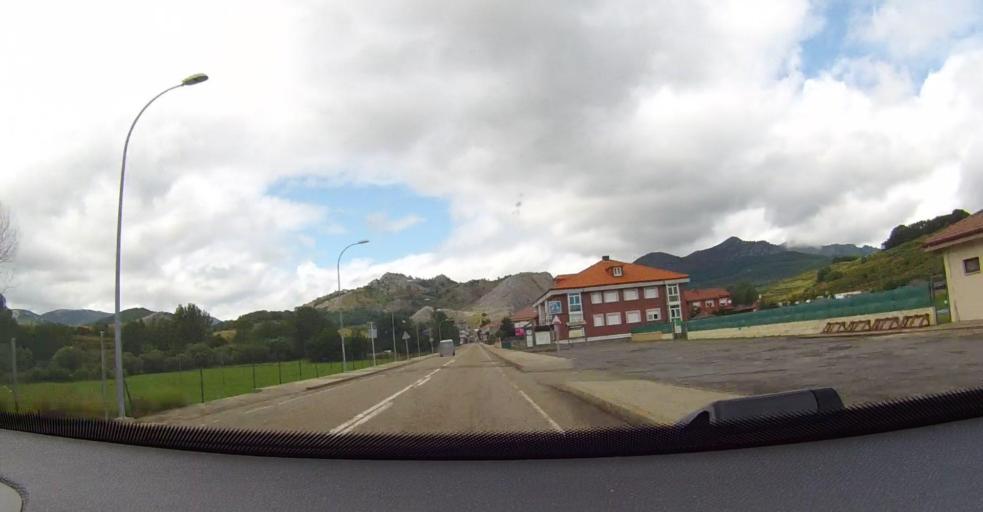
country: ES
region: Castille and Leon
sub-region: Provincia de Leon
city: Puebla de Lillo
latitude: 43.0040
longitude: -5.2684
